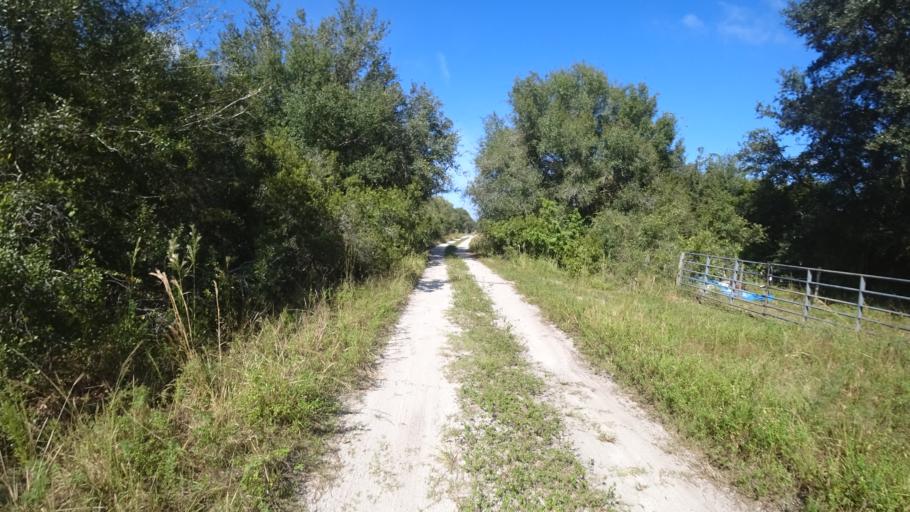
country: US
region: Florida
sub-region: DeSoto County
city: Arcadia
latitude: 27.2896
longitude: -82.0643
